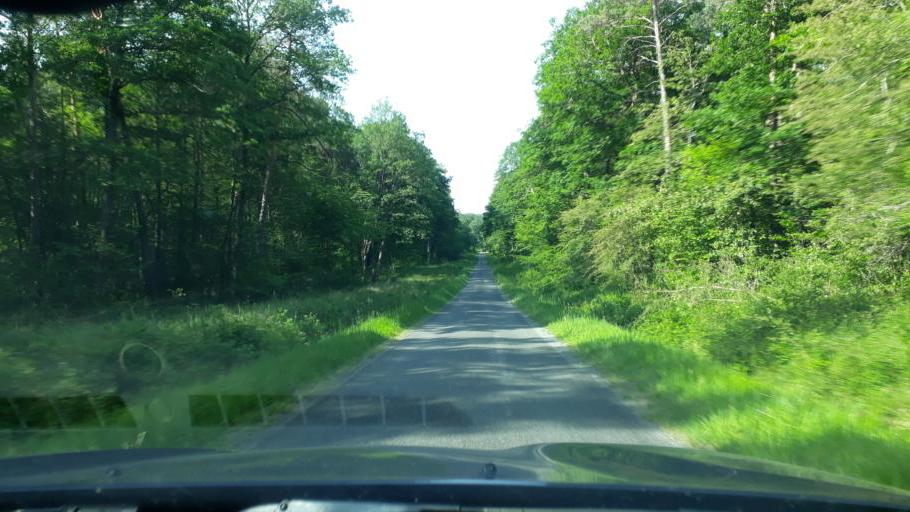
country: FR
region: Centre
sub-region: Departement du Loiret
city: Dadonville
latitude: 48.0497
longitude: 2.2711
